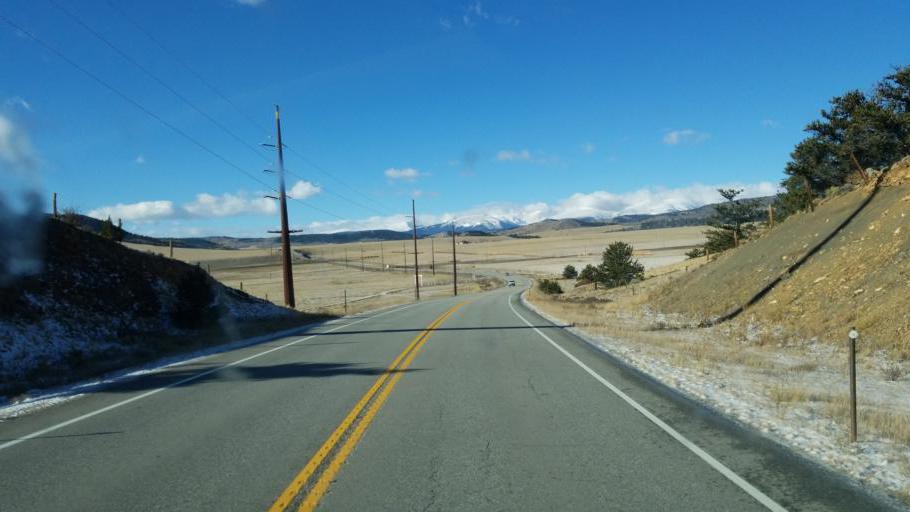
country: US
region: Colorado
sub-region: Park County
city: Fairplay
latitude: 39.2987
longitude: -105.8974
